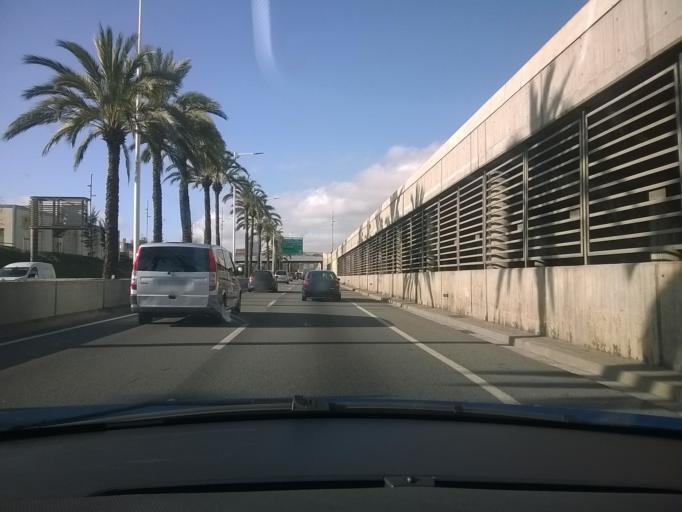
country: ES
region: Catalonia
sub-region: Provincia de Barcelona
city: Sant Marti
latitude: 41.4026
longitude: 2.2134
